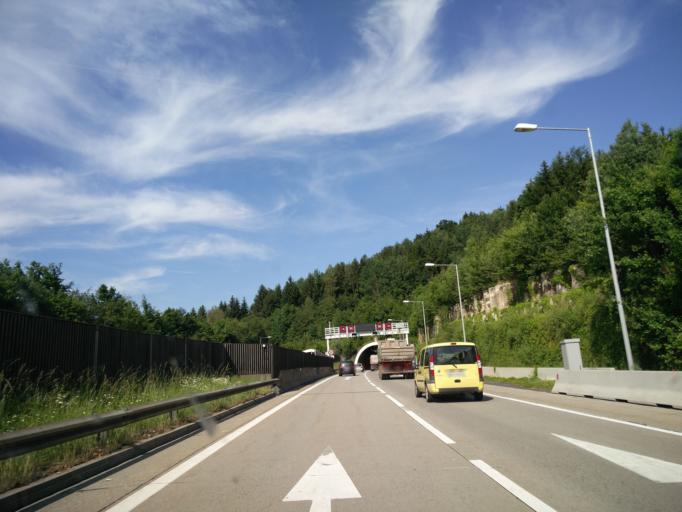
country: AT
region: Carinthia
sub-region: Klagenfurt am Woerthersee
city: Klagenfurt am Woerthersee
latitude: 46.6346
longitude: 14.2451
